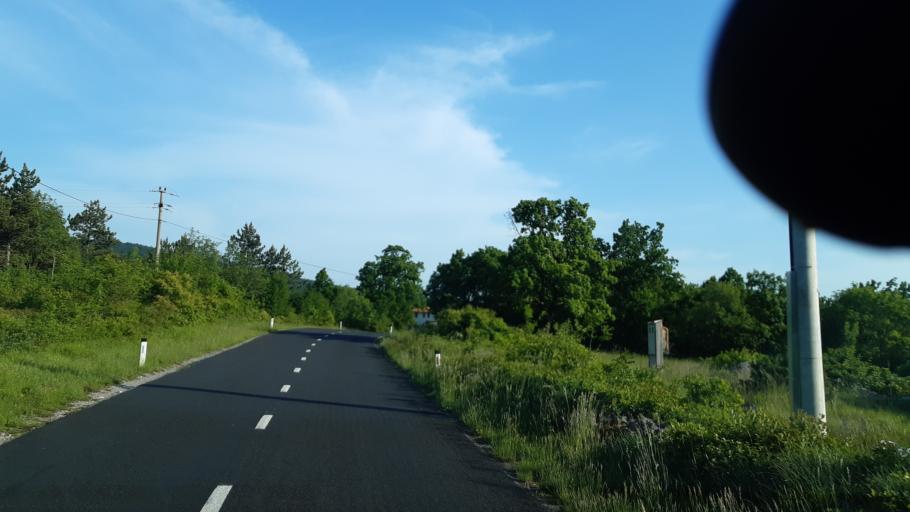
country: SI
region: Sezana
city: Sezana
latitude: 45.7443
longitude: 13.9281
